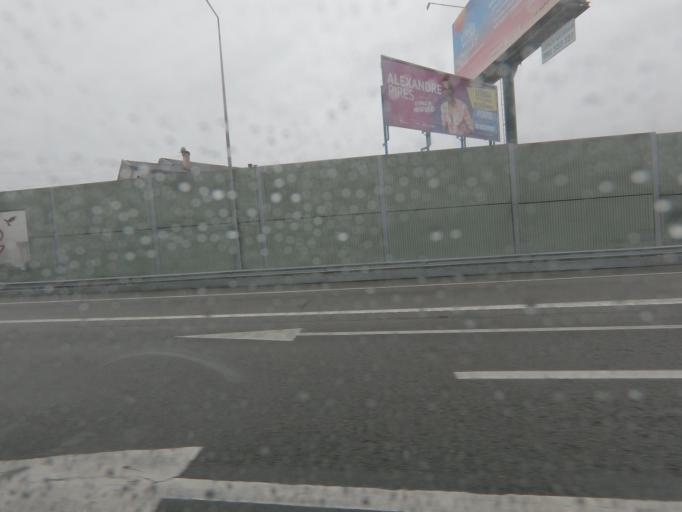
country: PT
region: Porto
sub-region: Maia
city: Pedroucos
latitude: 41.1927
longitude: -8.5921
